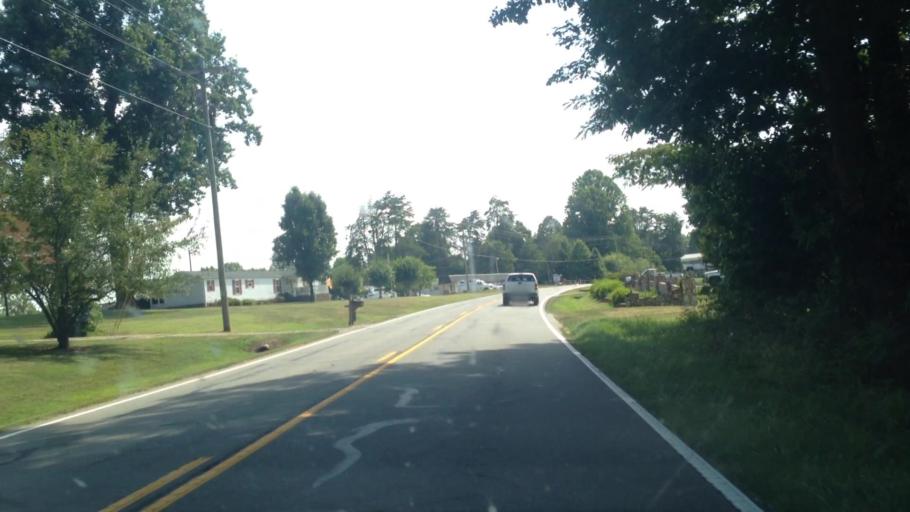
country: US
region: North Carolina
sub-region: Stokes County
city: Walnut Cove
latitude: 36.2660
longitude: -80.0927
